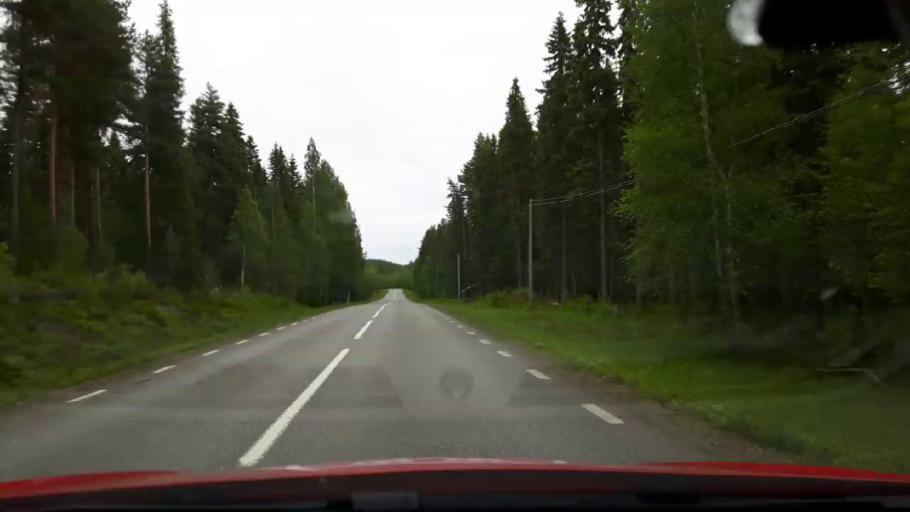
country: SE
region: Jaemtland
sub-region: Stroemsunds Kommun
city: Stroemsund
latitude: 63.3955
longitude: 15.6552
